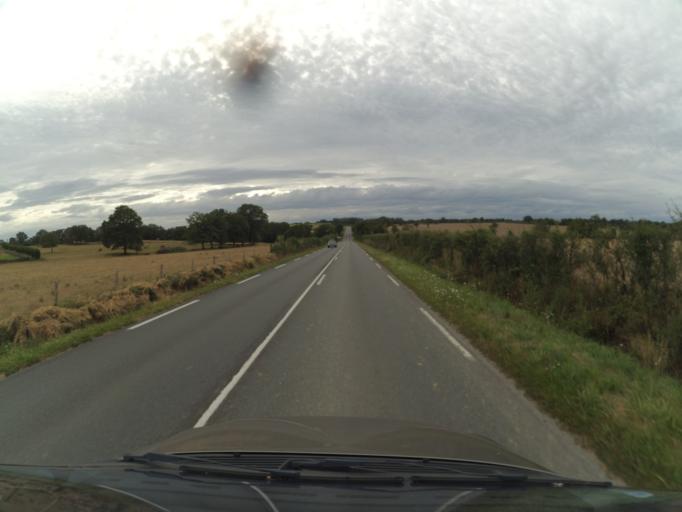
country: FR
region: Pays de la Loire
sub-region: Departement de la Vendee
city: Saint-Aubin-des-Ormeaux
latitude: 47.0169
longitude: -1.0038
